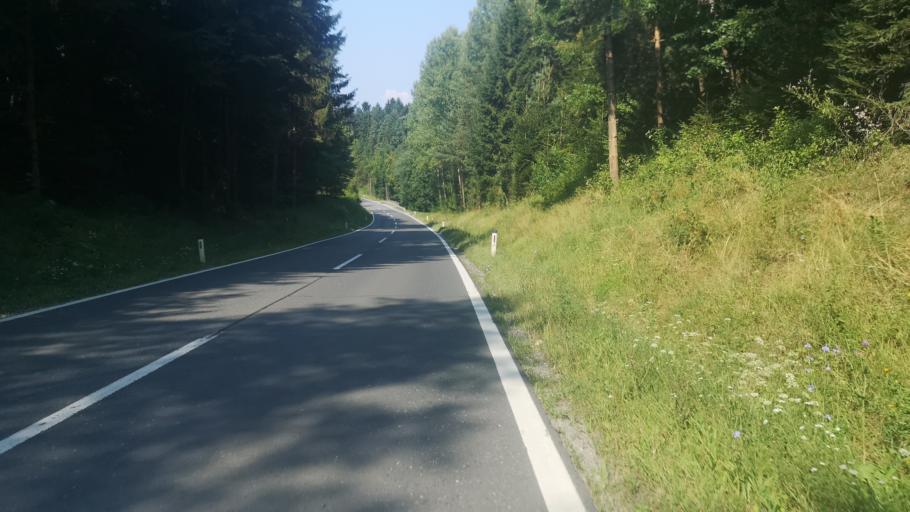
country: AT
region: Styria
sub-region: Politischer Bezirk Graz-Umgebung
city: Unterpremstatten
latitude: 46.9744
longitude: 15.3858
